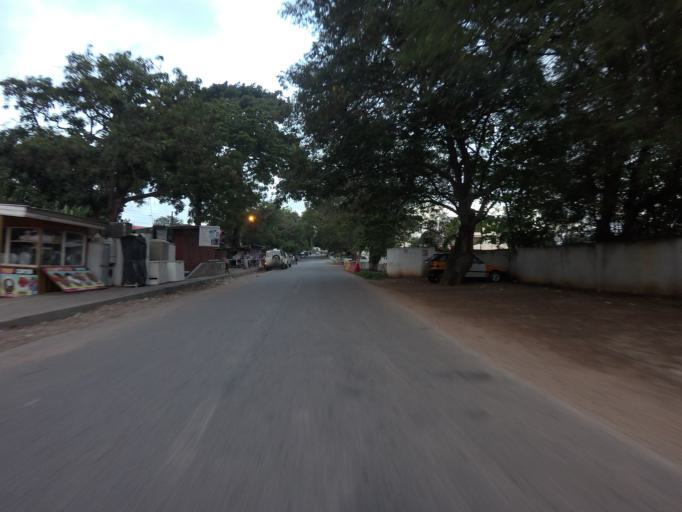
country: GH
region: Greater Accra
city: Accra
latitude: 5.5723
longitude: -0.1862
